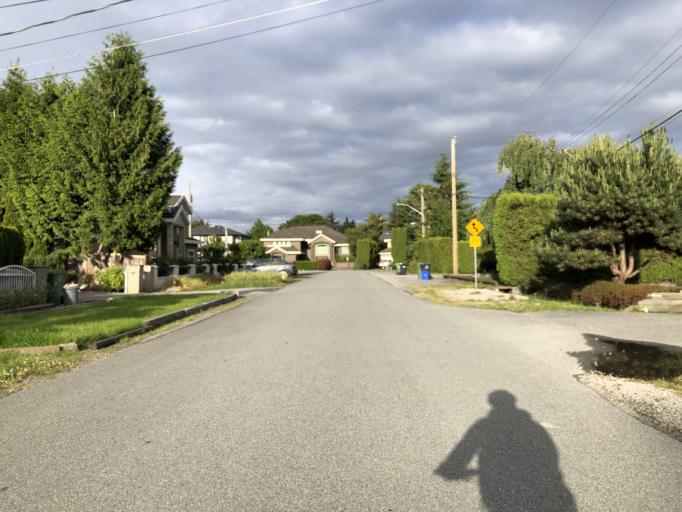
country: CA
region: British Columbia
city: Richmond
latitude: 49.1418
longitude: -123.1223
